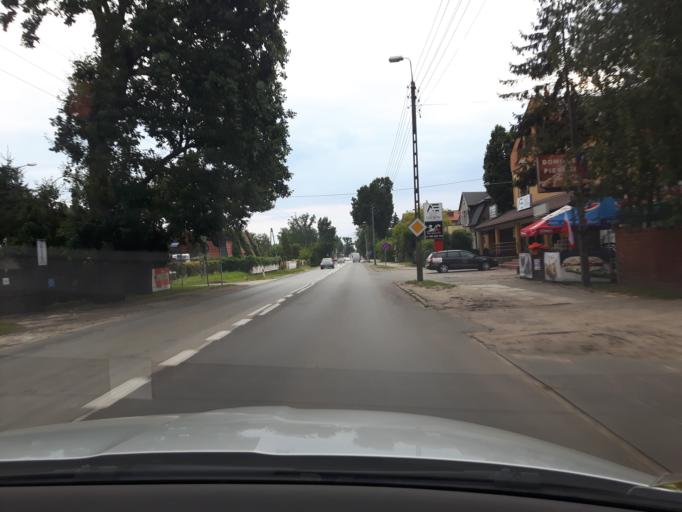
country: PL
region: Masovian Voivodeship
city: Zielonka
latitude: 52.3017
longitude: 21.1564
